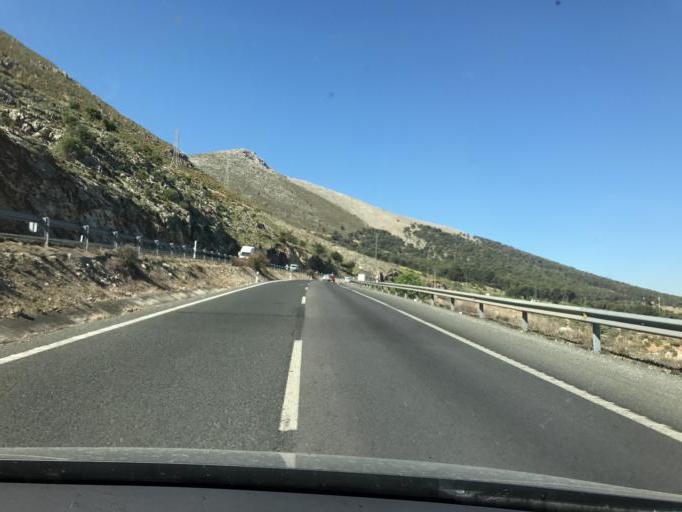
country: ES
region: Andalusia
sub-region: Provincia de Granada
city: Loja
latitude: 37.1601
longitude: -4.1429
